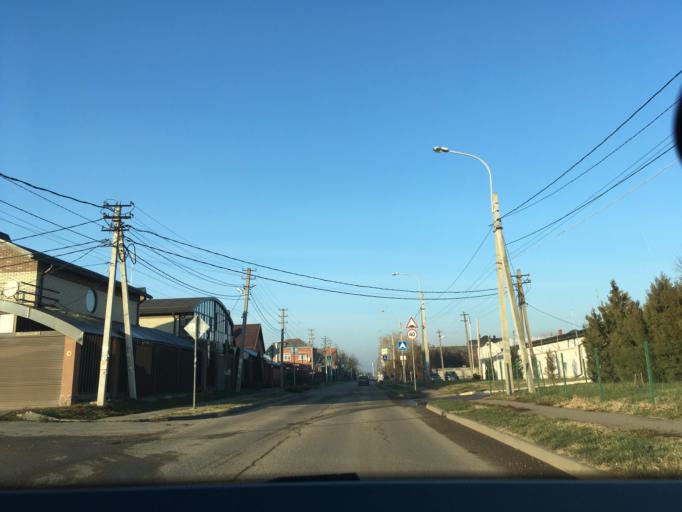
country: RU
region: Krasnodarskiy
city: Krasnodar
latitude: 45.1186
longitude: 39.0145
